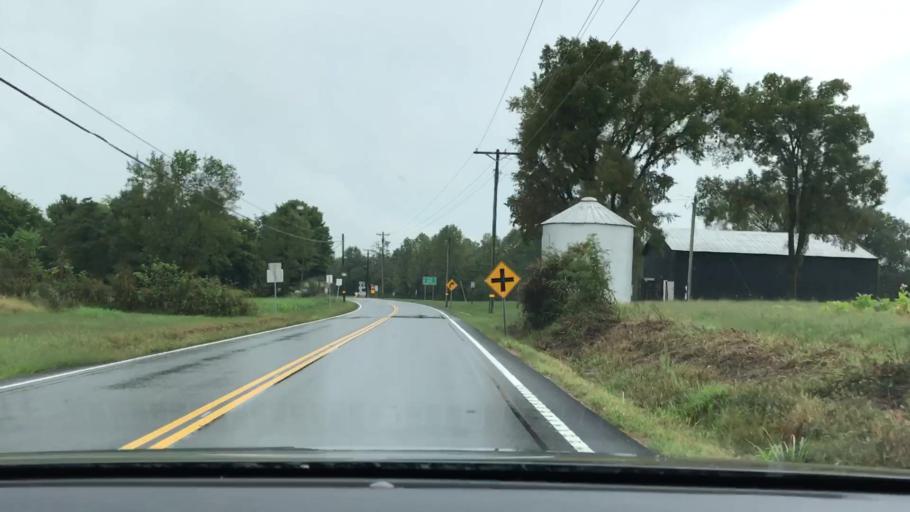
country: US
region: Tennessee
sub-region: Macon County
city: Red Boiling Springs
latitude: 36.4506
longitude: -85.8809
